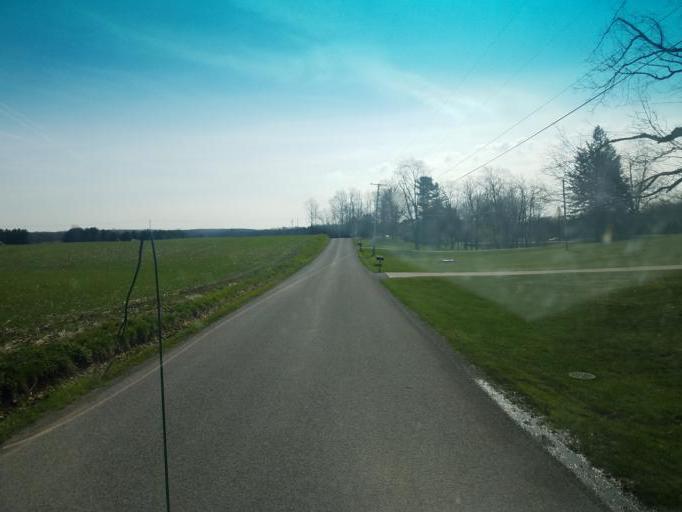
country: US
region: Ohio
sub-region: Richland County
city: Lincoln Heights
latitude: 40.8802
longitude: -82.5160
